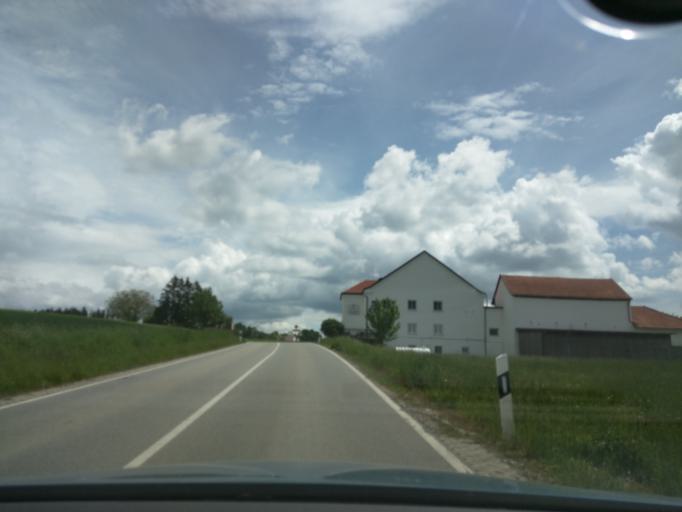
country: DE
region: Bavaria
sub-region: Lower Bavaria
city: Furstenzell
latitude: 48.5303
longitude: 13.3460
